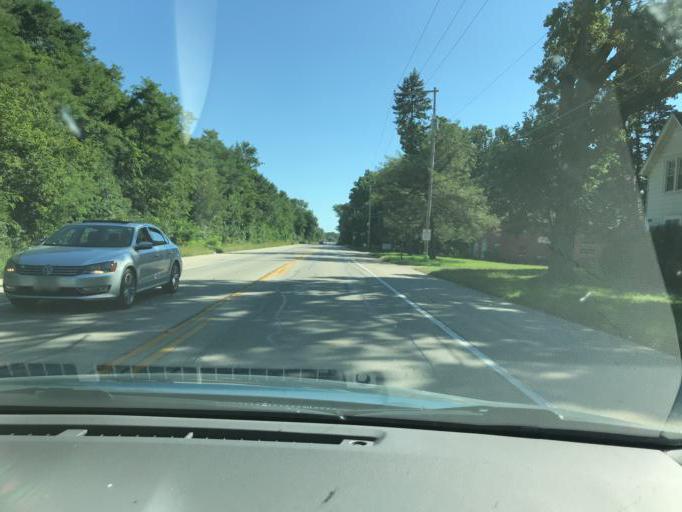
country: US
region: Illinois
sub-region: Lake County
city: Winthrop Harbor
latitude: 42.5035
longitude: -87.8231
